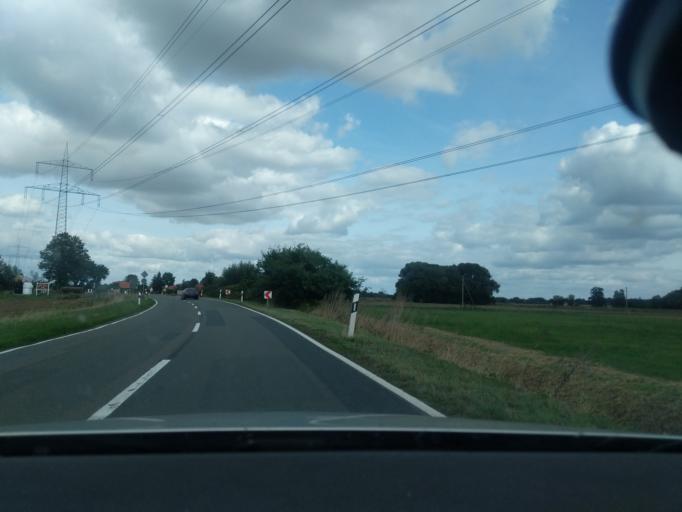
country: DE
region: Lower Saxony
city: Warpe
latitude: 52.7676
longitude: 9.1007
